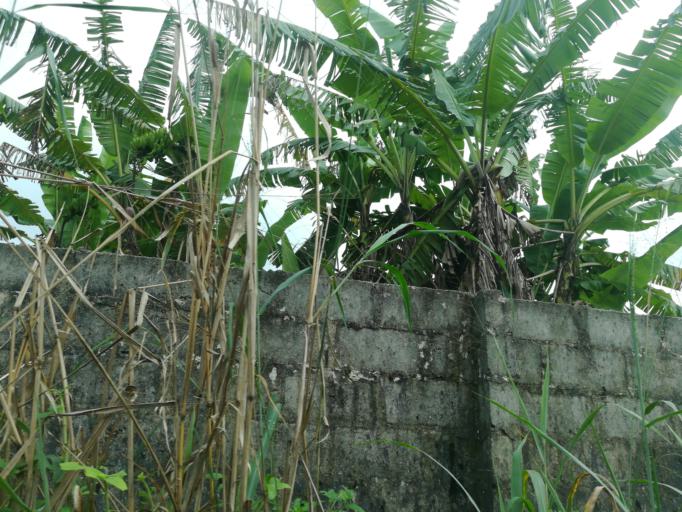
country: NG
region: Rivers
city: Emuoha
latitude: 4.8927
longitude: 6.9737
